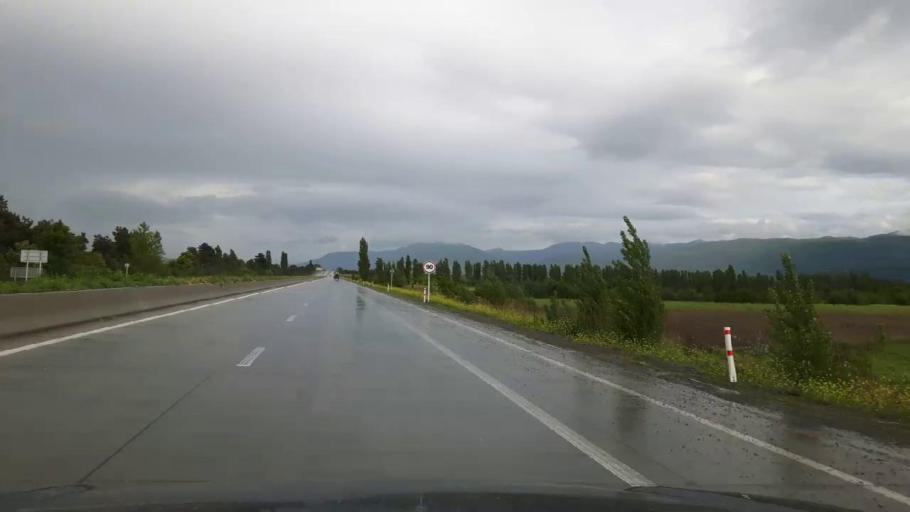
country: GE
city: Agara
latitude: 42.0458
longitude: 43.9192
